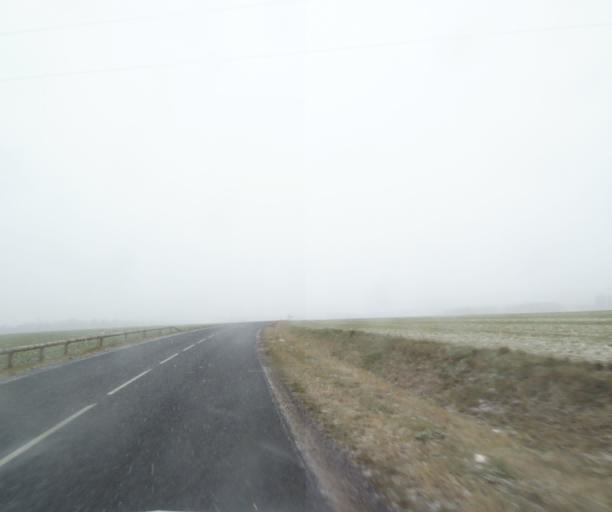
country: FR
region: Champagne-Ardenne
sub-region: Departement de la Haute-Marne
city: Wassy
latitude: 48.5095
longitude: 4.9951
